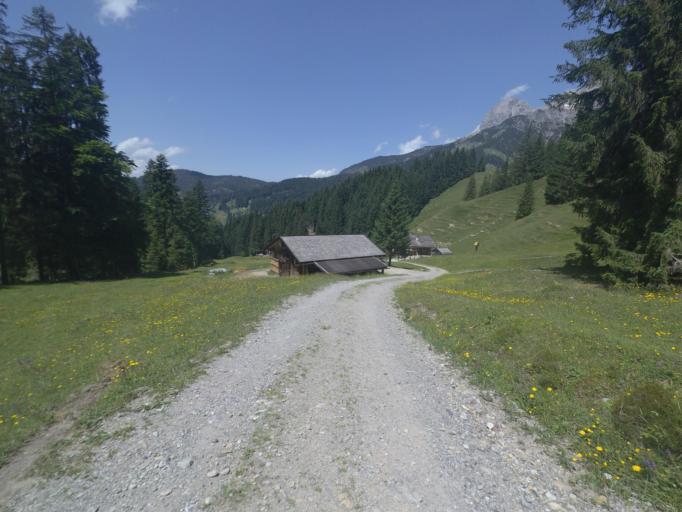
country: AT
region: Salzburg
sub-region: Politischer Bezirk Zell am See
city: Dienten am Hochkonig
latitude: 47.4113
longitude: 12.9955
